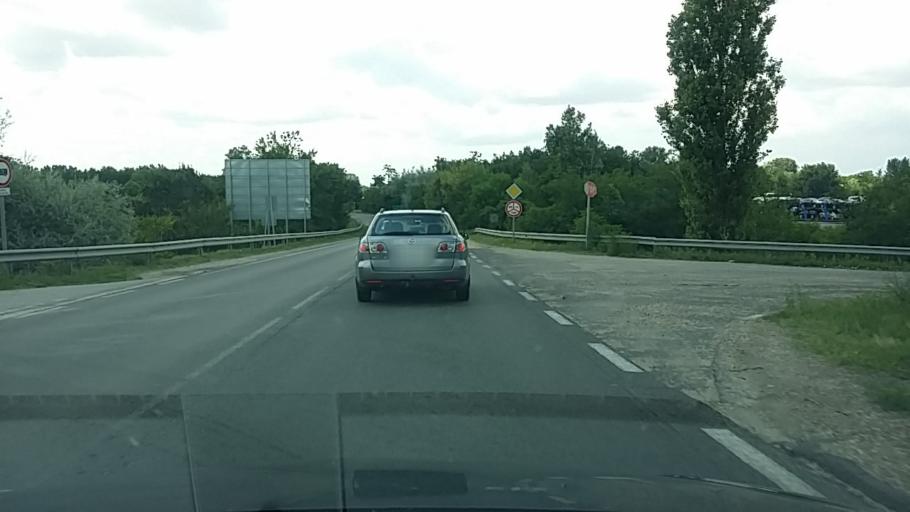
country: HU
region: Bacs-Kiskun
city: Lajosmizse
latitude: 46.9925
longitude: 19.6061
